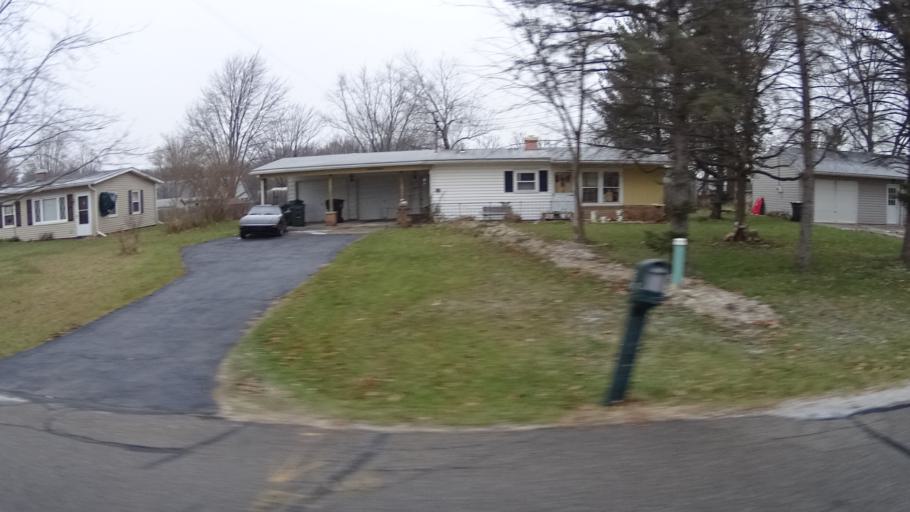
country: US
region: Ohio
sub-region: Lorain County
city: Eaton Estates
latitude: 41.3110
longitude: -82.0083
